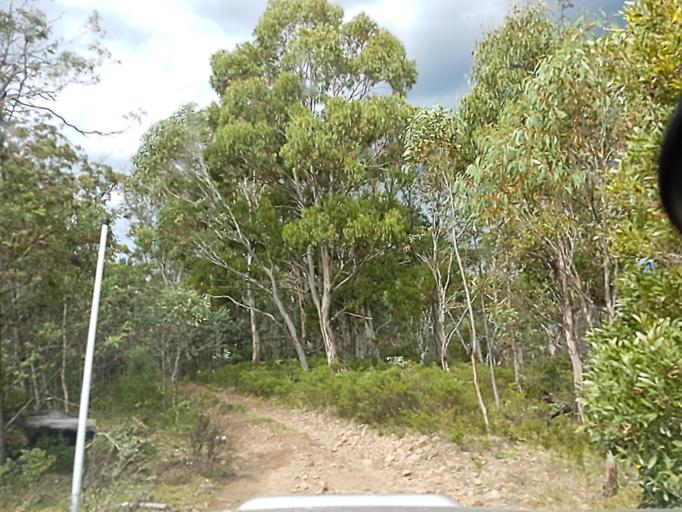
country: AU
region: New South Wales
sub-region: Snowy River
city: Jindabyne
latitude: -36.8797
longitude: 148.1861
